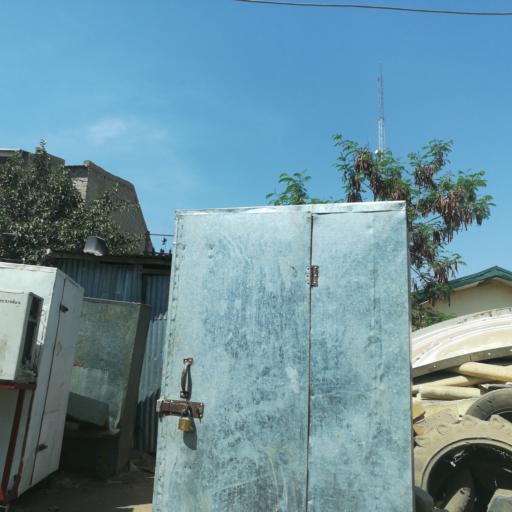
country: NG
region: Kano
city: Kano
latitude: 12.0057
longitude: 8.5361
